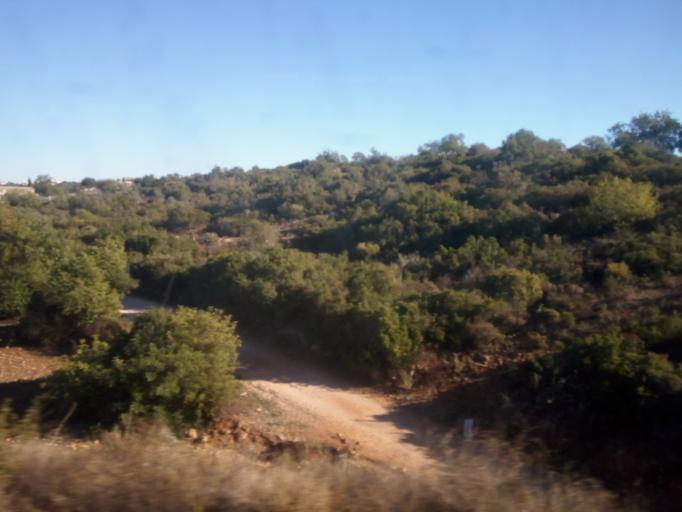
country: PT
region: Faro
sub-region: Albufeira
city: Ferreiras
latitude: 37.1420
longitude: -8.2520
